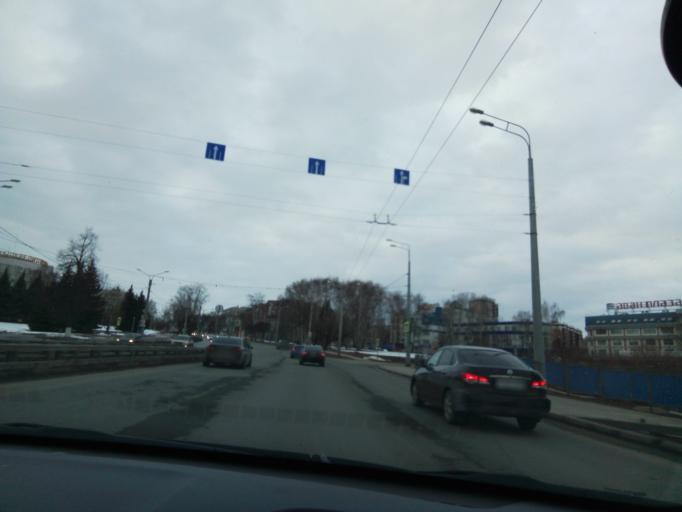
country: RU
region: Chuvashia
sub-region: Cheboksarskiy Rayon
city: Cheboksary
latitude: 56.1457
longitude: 47.2392
